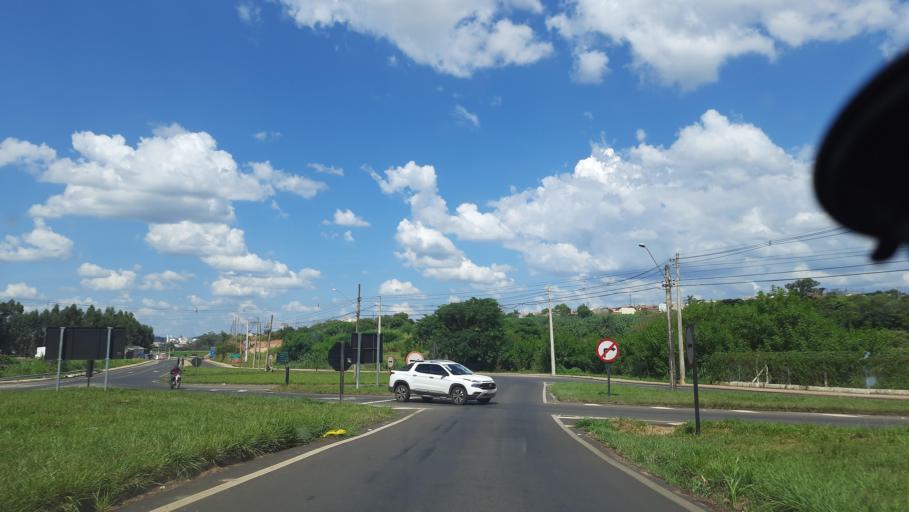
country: BR
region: Sao Paulo
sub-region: Sao Jose Do Rio Pardo
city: Sao Jose do Rio Pardo
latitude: -21.6036
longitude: -46.9160
